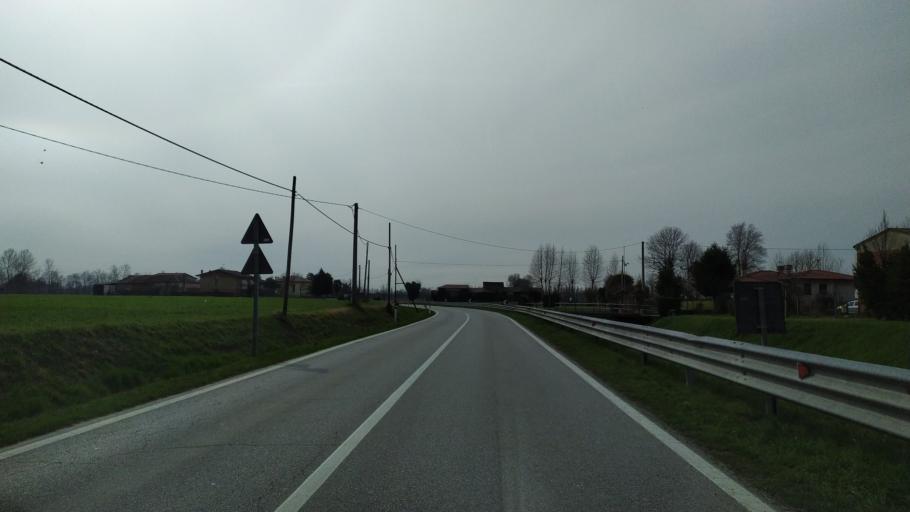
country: IT
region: Veneto
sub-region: Provincia di Padova
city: Villa del Conte
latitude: 45.5734
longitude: 11.8634
